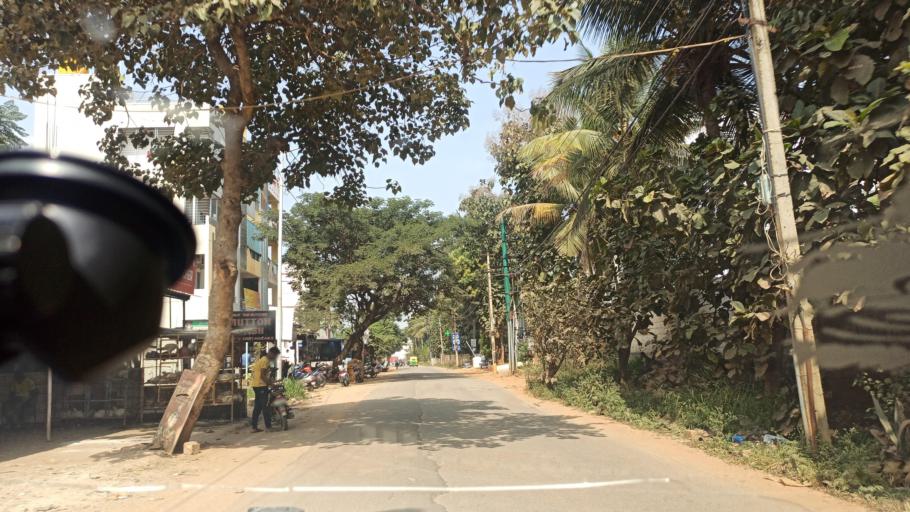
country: IN
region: Karnataka
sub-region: Bangalore Urban
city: Yelahanka
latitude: 13.0987
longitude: 77.6173
